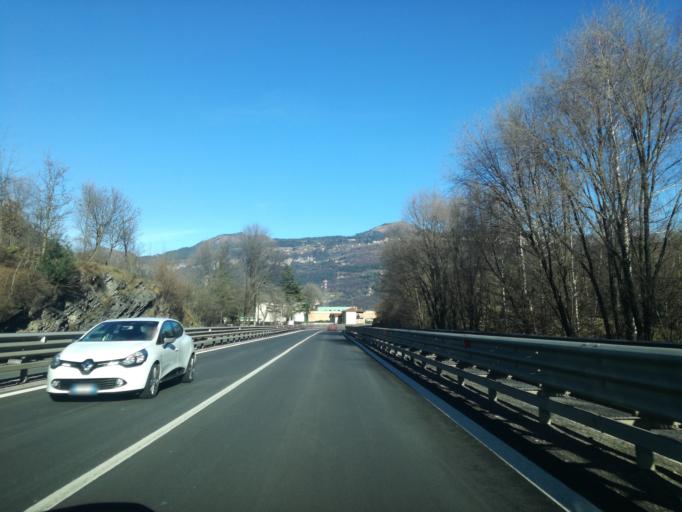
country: IT
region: Lombardy
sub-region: Provincia di Bergamo
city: Sovere
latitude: 45.8020
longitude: 10.0207
